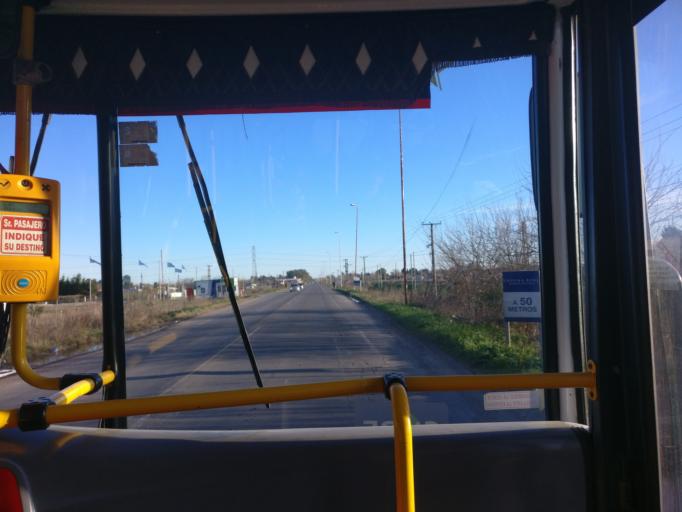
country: AR
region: Buenos Aires
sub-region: Partido de Ezeiza
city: Ezeiza
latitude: -34.9258
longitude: -58.6110
